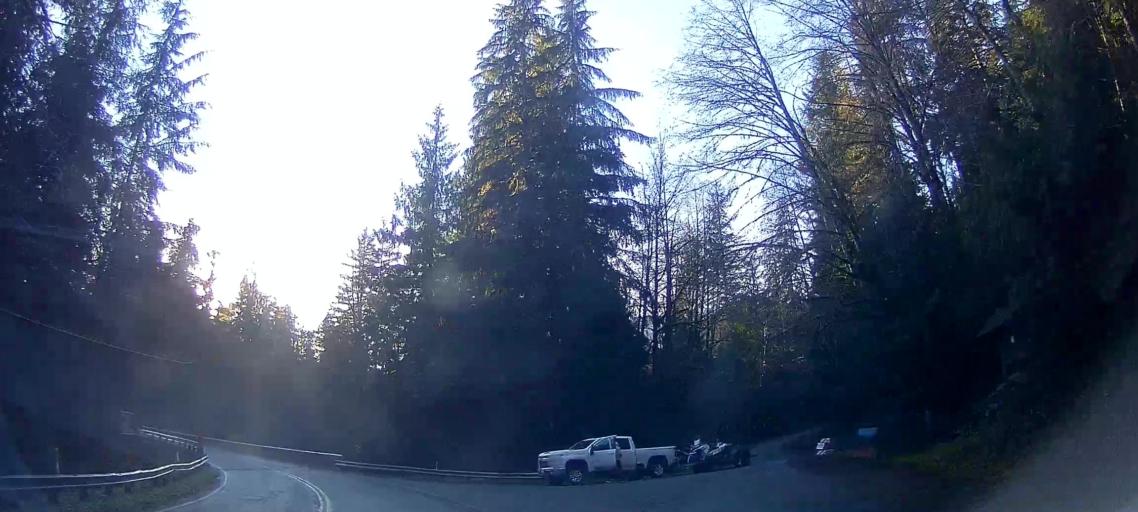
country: US
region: Washington
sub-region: Snohomish County
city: Darrington
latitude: 48.6492
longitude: -121.7284
